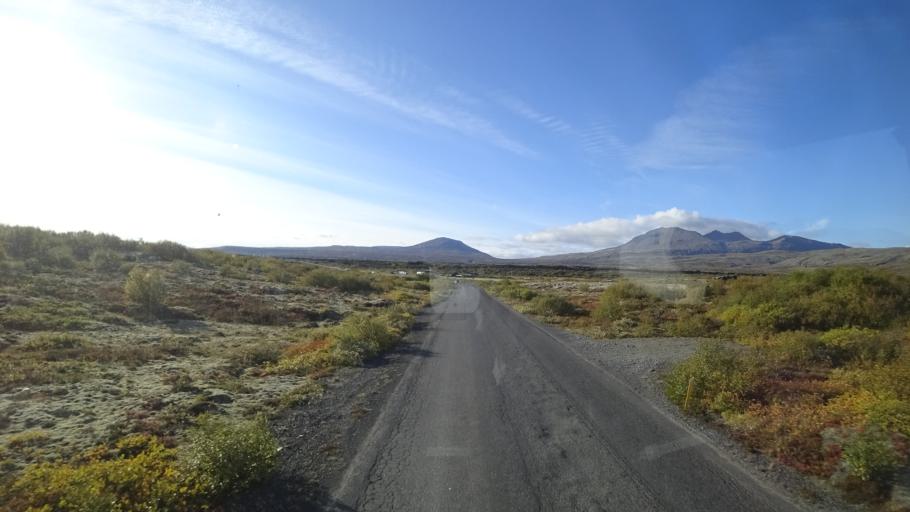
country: IS
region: South
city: Hveragerdi
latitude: 64.2785
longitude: -21.0806
